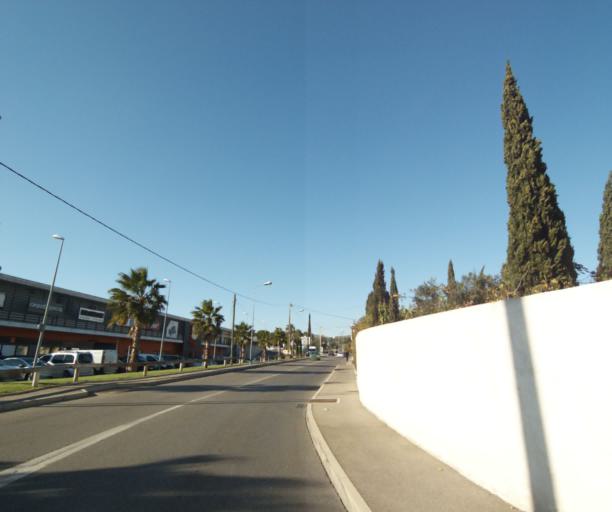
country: FR
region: Provence-Alpes-Cote d'Azur
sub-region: Departement des Bouches-du-Rhone
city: La Ciotat
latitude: 43.1882
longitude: 5.6052
